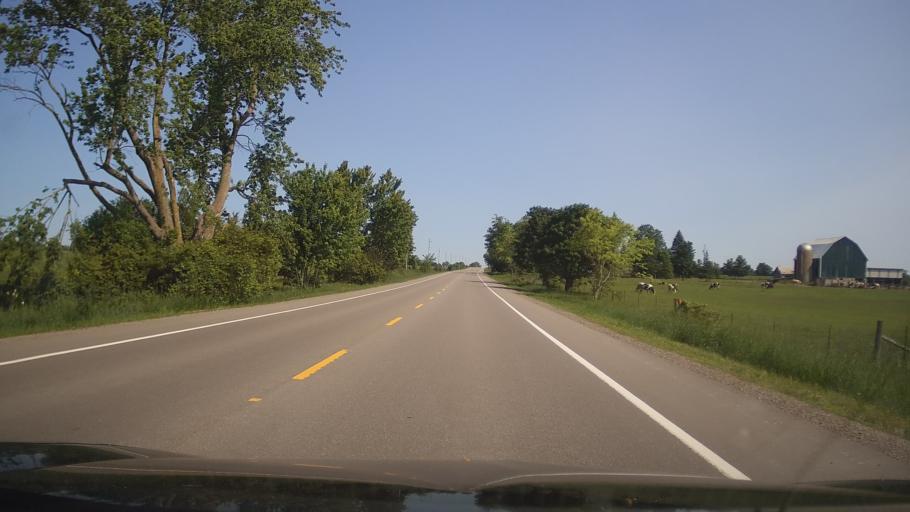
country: CA
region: Ontario
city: Omemee
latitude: 44.3606
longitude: -78.8920
